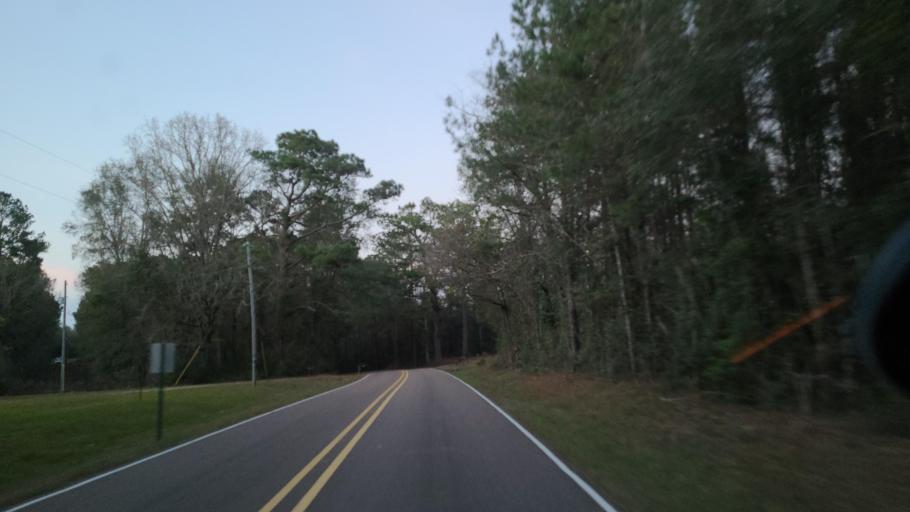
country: US
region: Mississippi
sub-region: Forrest County
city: Hattiesburg
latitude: 31.2258
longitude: -89.2355
